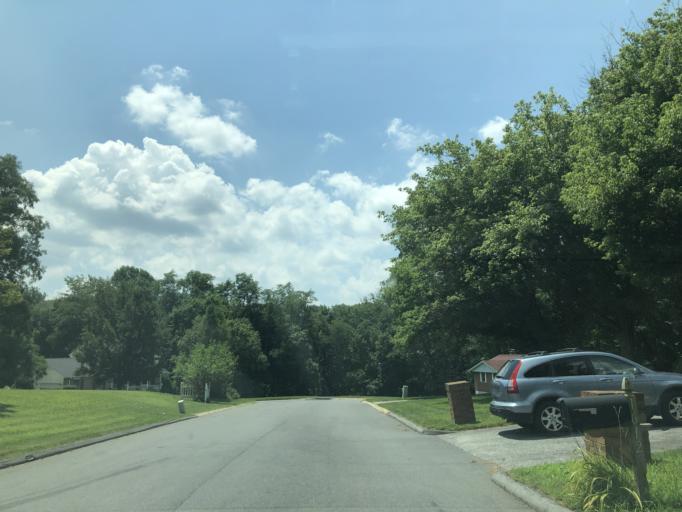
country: US
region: Maryland
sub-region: Carroll County
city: Westminster
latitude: 39.5296
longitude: -76.9347
